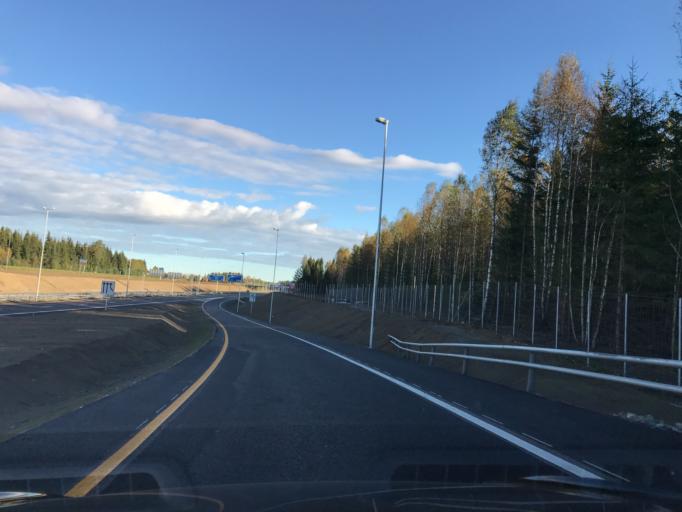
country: NO
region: Akershus
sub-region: Ullensaker
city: Jessheim
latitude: 60.1597
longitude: 11.1544
